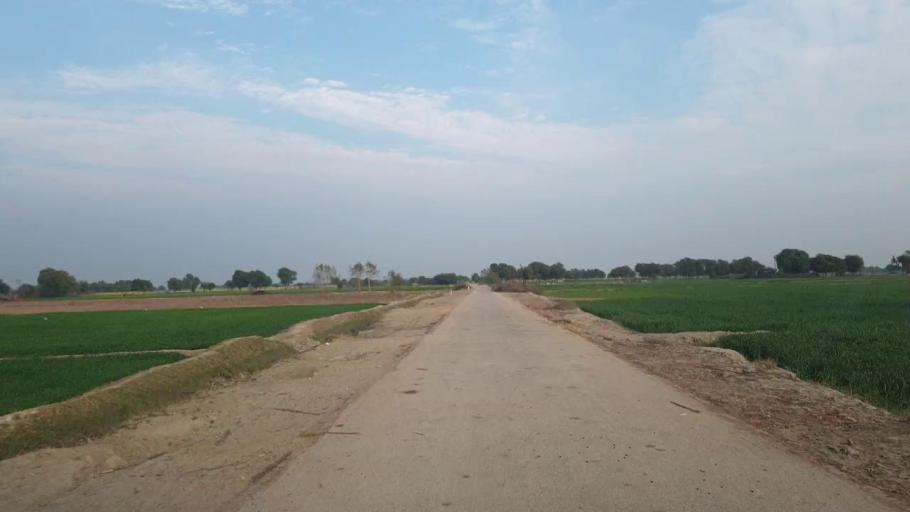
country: PK
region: Sindh
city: Shahpur Chakar
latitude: 26.0978
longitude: 68.5426
